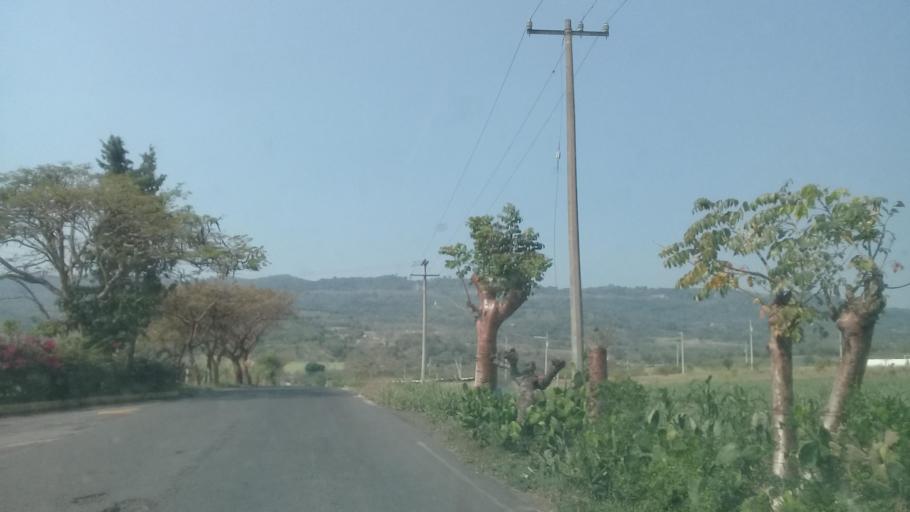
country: MX
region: Veracruz
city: El Castillo
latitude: 19.5847
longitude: -96.8271
